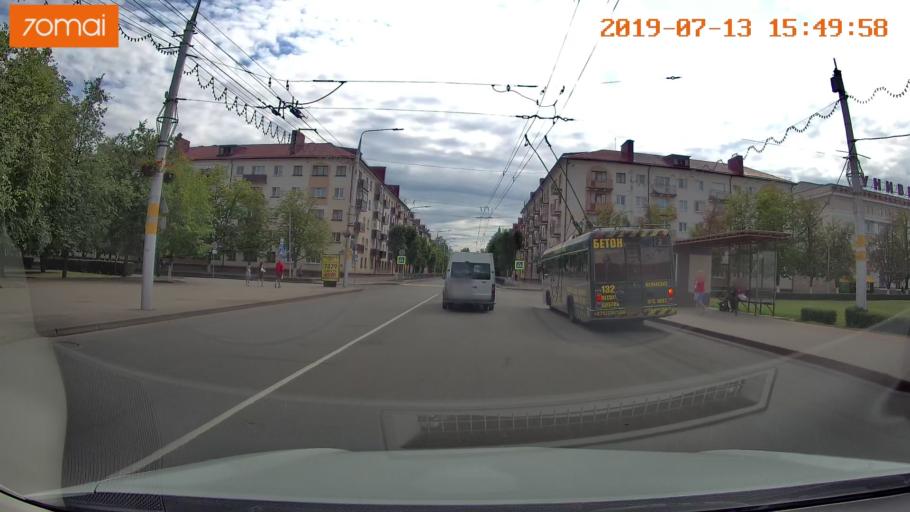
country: BY
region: Mogilev
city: Babruysk
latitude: 53.1450
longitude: 29.2271
